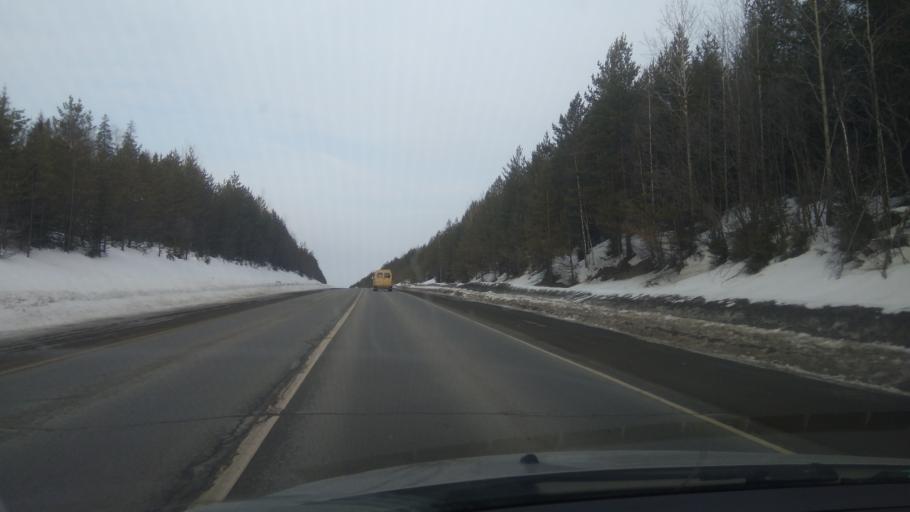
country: RU
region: Sverdlovsk
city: Nizhniye Sergi
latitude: 56.8233
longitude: 59.3226
